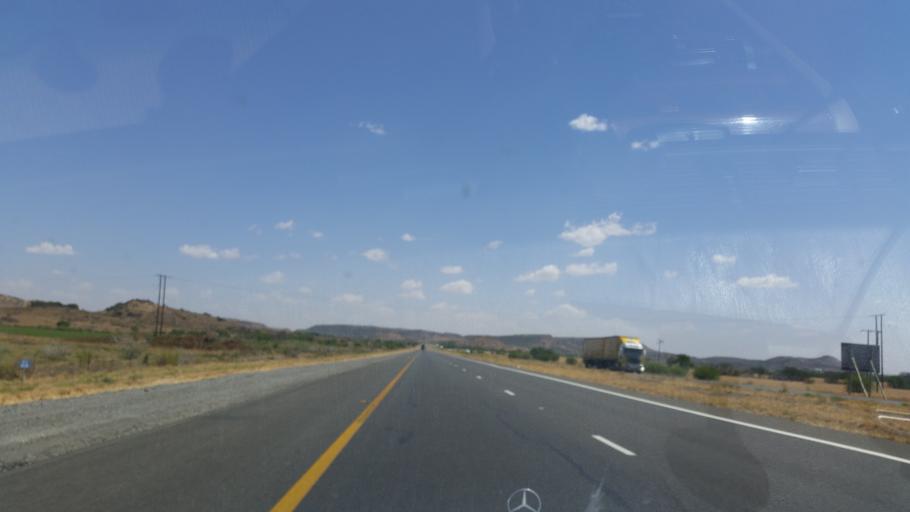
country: ZA
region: Orange Free State
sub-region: Mangaung Metropolitan Municipality
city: Bloemfontein
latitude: -28.9696
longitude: 26.3281
